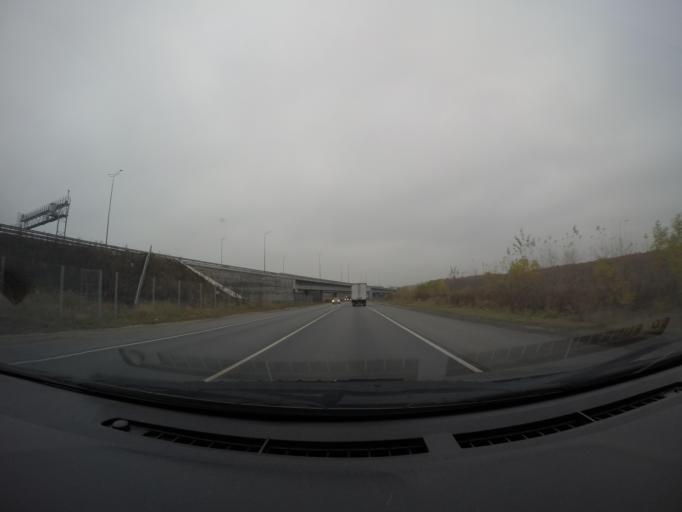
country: RU
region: Moskovskaya
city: Belyye Stolby
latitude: 55.3456
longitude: 37.8730
